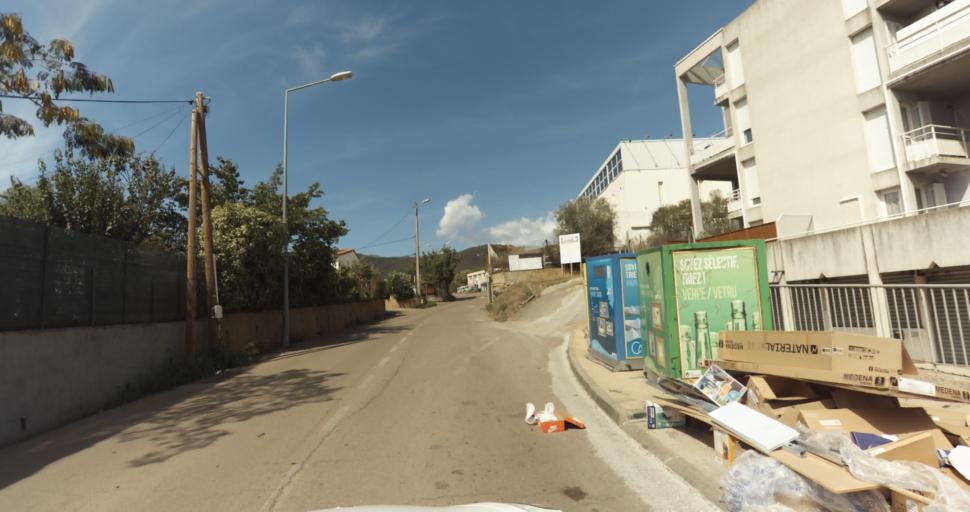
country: FR
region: Corsica
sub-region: Departement de la Corse-du-Sud
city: Afa
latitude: 41.9530
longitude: 8.7738
